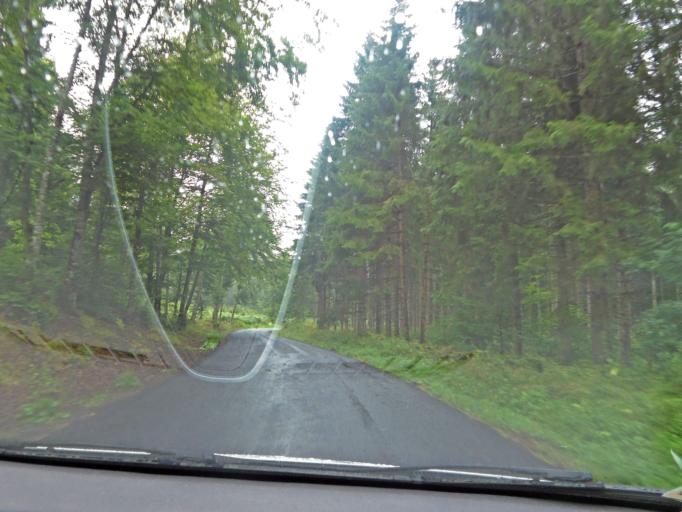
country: FR
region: Auvergne
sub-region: Departement du Puy-de-Dome
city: Orcines
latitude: 45.7529
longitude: 2.9305
